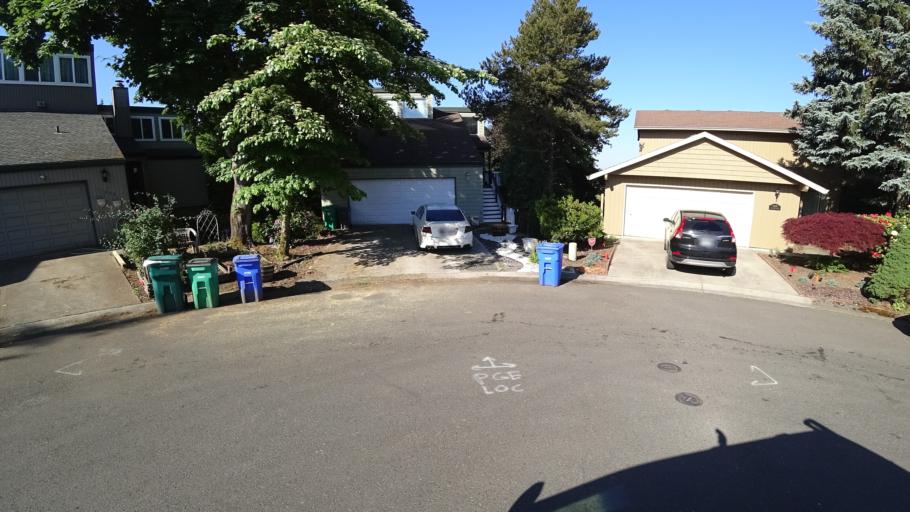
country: US
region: Oregon
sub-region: Multnomah County
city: Lents
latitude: 45.4698
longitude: -122.5446
